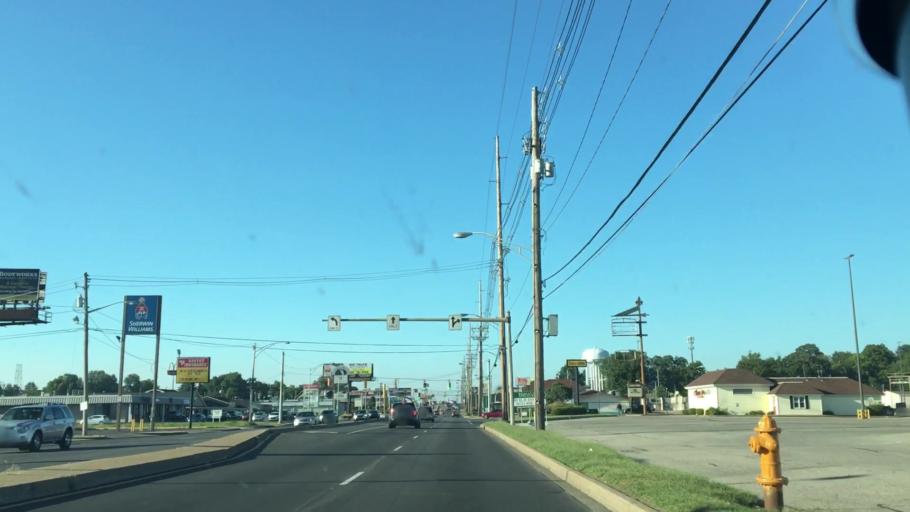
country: US
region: Indiana
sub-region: Vanderburgh County
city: Evansville
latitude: 37.9650
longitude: -87.4926
